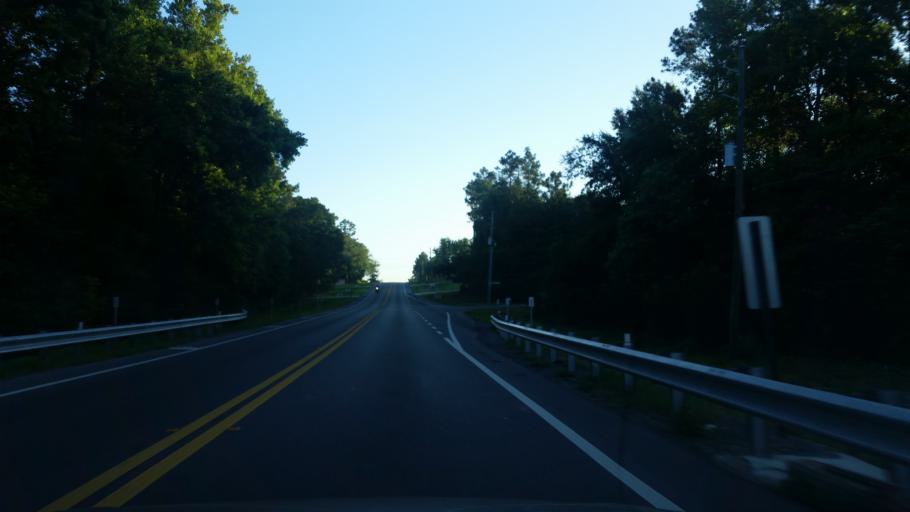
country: US
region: Florida
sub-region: Escambia County
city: Gonzalez
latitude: 30.5630
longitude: -87.3288
